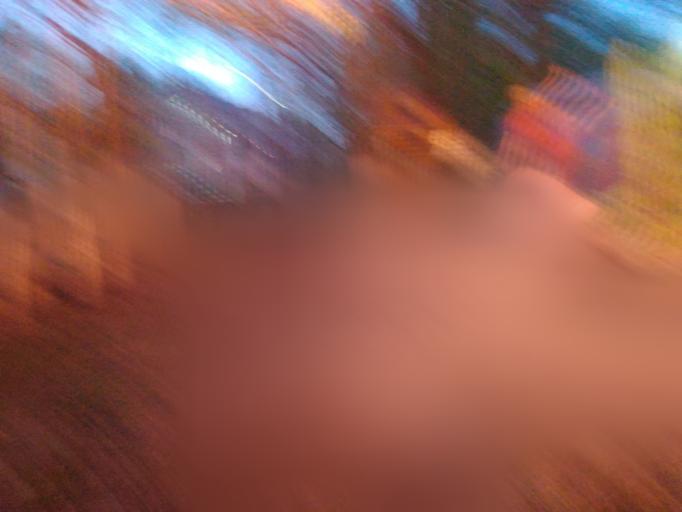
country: RU
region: Ulyanovsk
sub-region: Ulyanovskiy Rayon
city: Ulyanovsk
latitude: 54.2755
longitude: 48.3404
